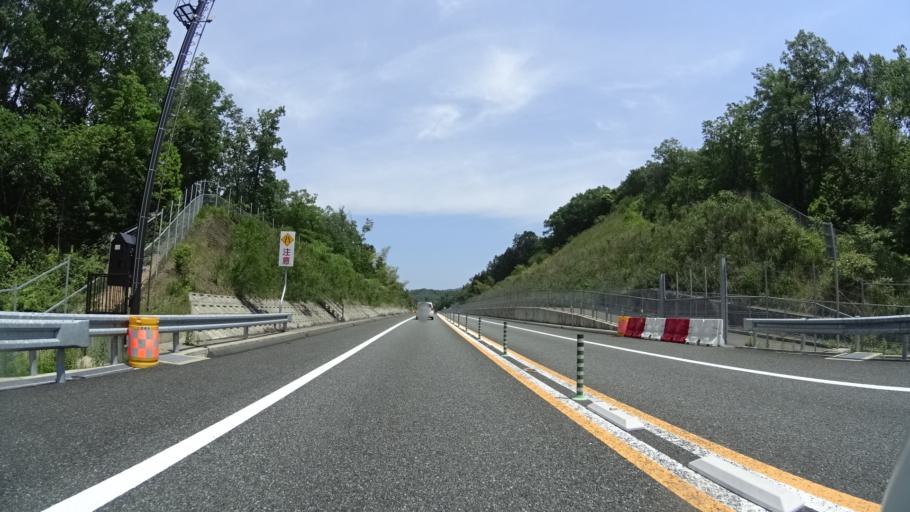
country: JP
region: Kyoto
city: Miyazu
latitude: 35.5689
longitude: 135.1208
